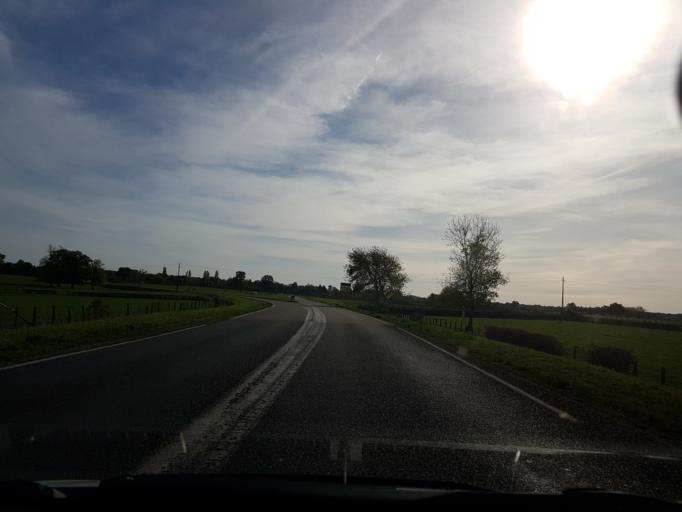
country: FR
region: Bourgogne
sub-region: Departement de l'Yonne
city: Avallon
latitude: 47.4885
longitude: 3.9896
